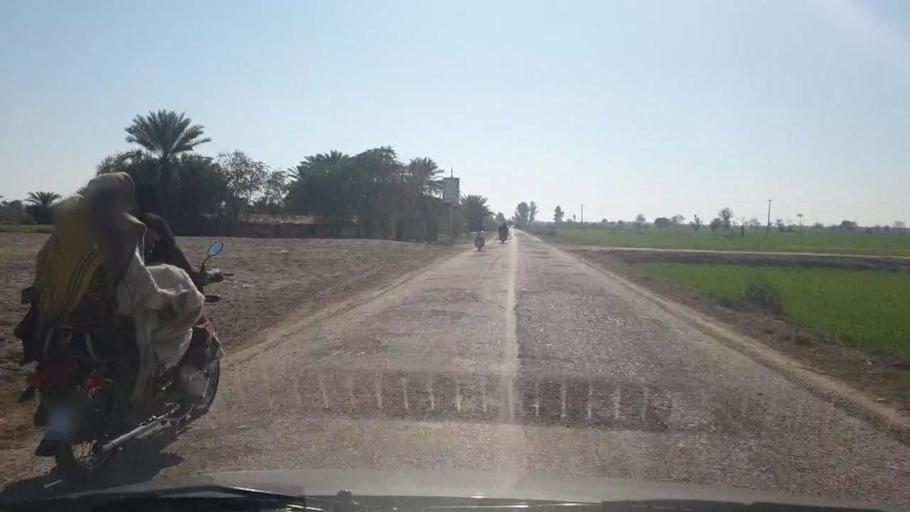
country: PK
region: Sindh
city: Bozdar
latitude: 27.1709
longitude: 68.6420
